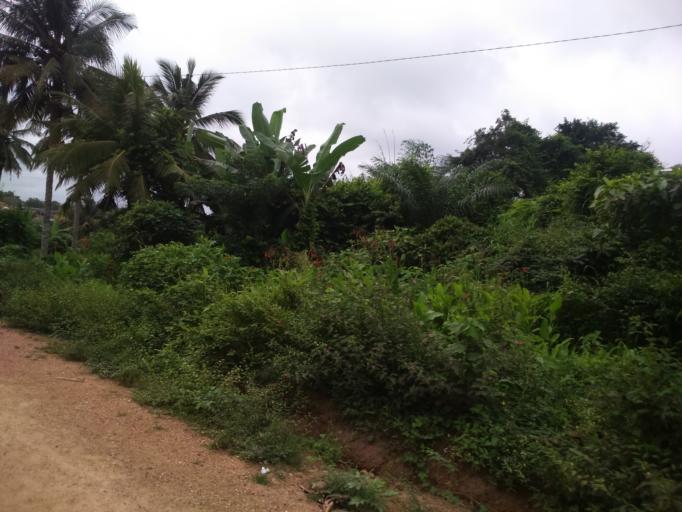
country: CI
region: Lagunes
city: Agou
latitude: 6.0561
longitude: -4.0980
